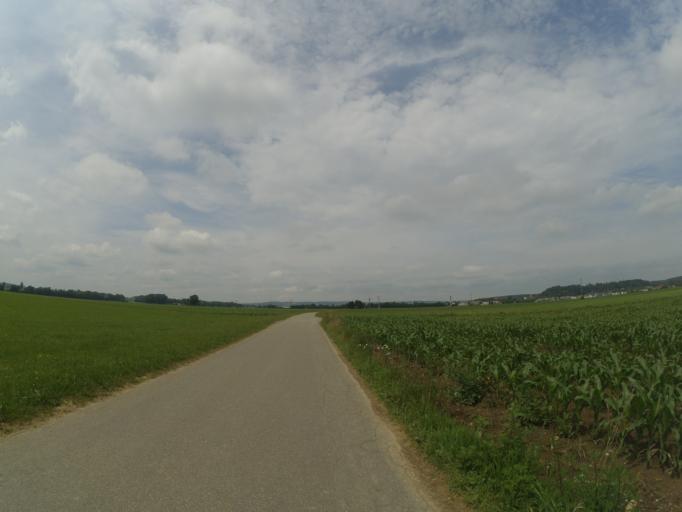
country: DE
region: Baden-Wuerttemberg
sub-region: Tuebingen Region
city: Leutkirch im Allgau
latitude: 47.8091
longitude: 10.0215
